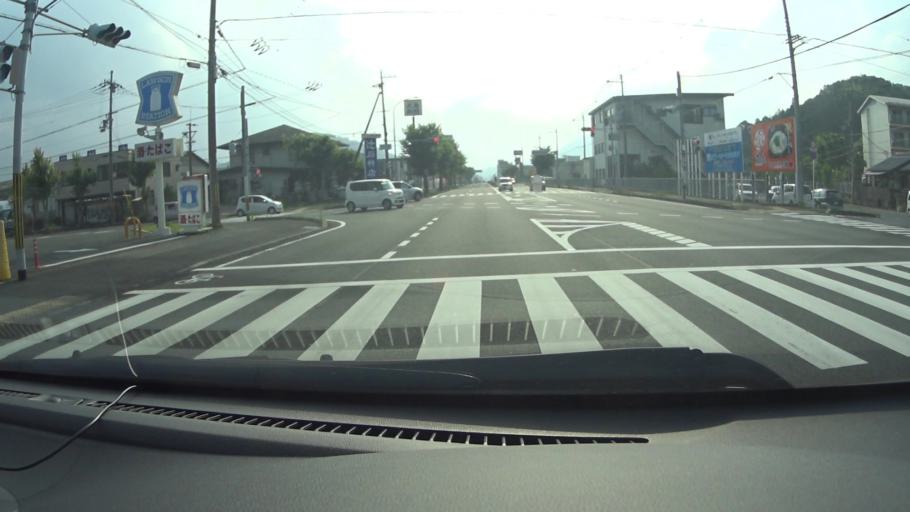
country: JP
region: Kyoto
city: Muko
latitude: 34.9772
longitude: 135.6588
